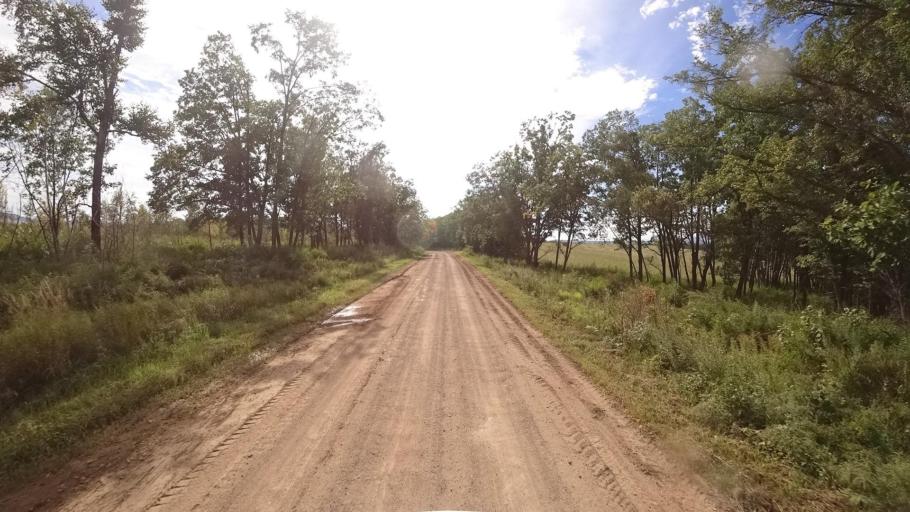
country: RU
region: Primorskiy
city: Dostoyevka
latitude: 44.3411
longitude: 133.5064
